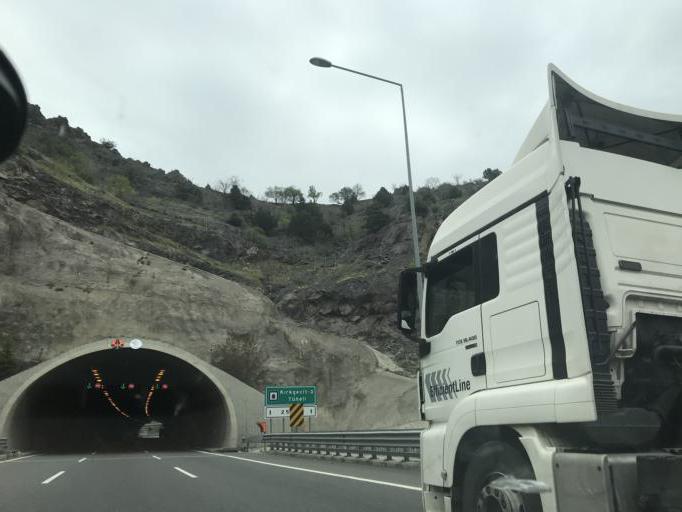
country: TR
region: Nigde
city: Ciftehan
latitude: 37.5576
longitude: 34.7651
